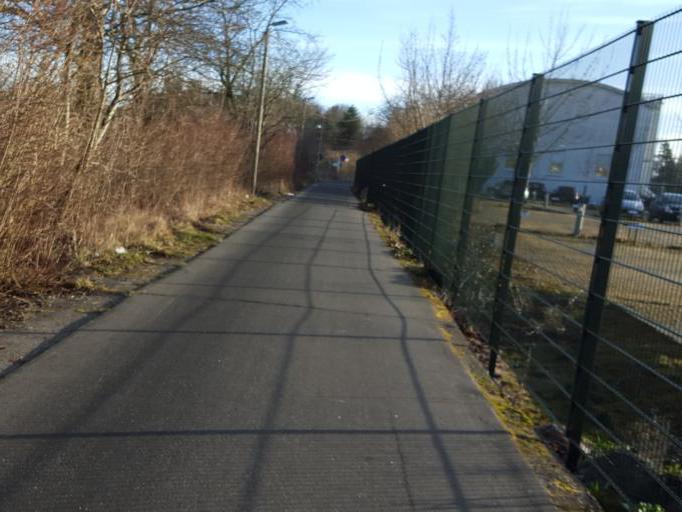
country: DK
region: North Denmark
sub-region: Alborg Kommune
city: Aalborg
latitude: 57.0380
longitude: 9.9187
